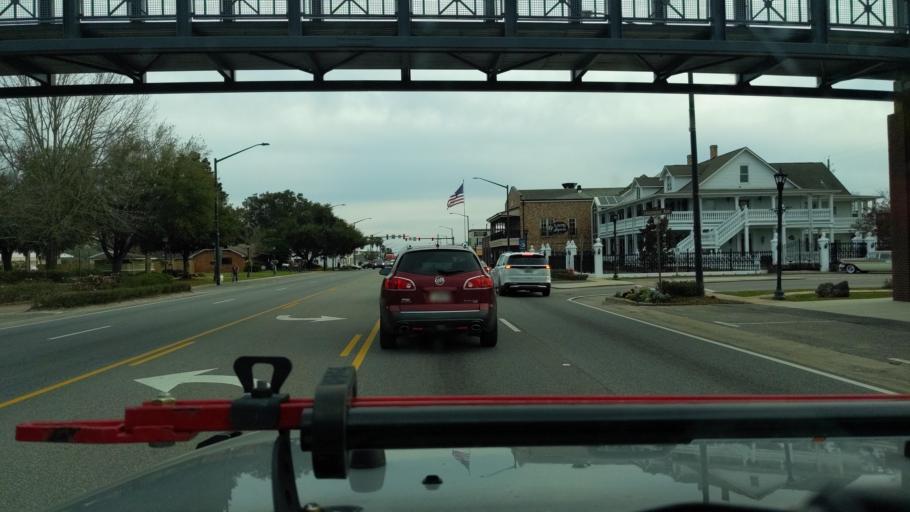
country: US
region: Alabama
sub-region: Baldwin County
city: Foley
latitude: 30.4078
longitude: -87.6838
